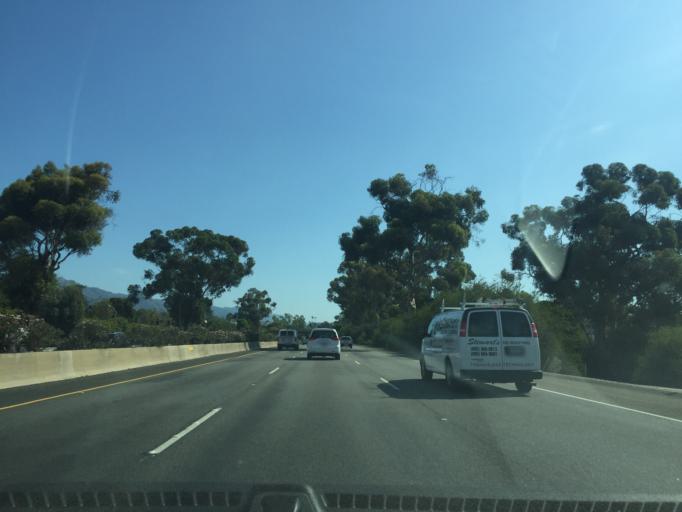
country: US
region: California
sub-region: Santa Barbara County
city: Mission Canyon
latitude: 34.4409
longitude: -119.7662
